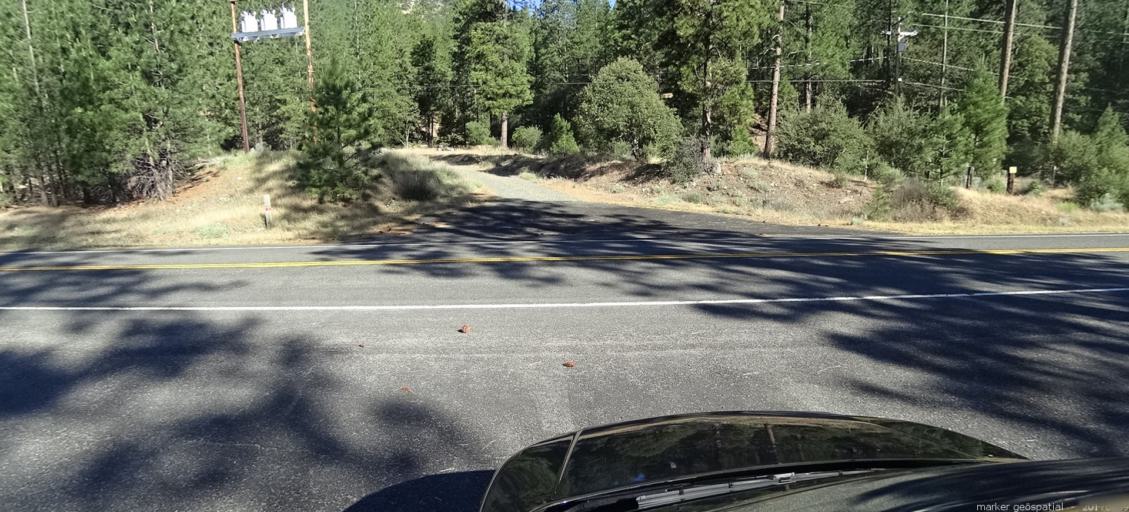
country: US
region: California
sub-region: Siskiyou County
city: Weed
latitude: 41.3082
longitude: -122.7729
